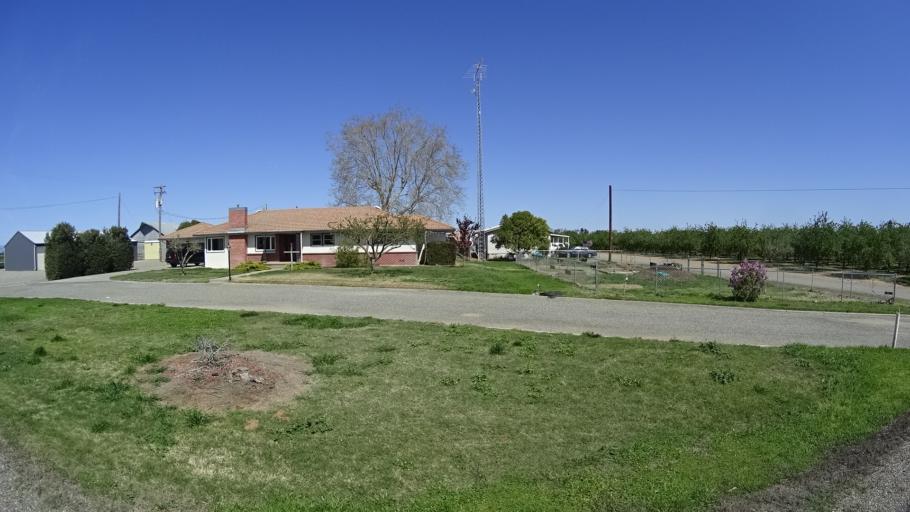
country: US
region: California
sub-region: Glenn County
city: Hamilton City
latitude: 39.7897
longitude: -122.1021
